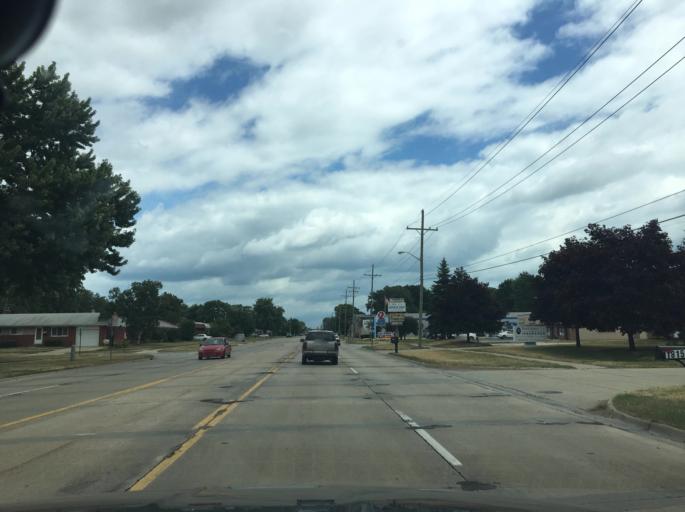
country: US
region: Michigan
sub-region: Macomb County
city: Fraser
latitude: 42.5244
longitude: -82.9342
